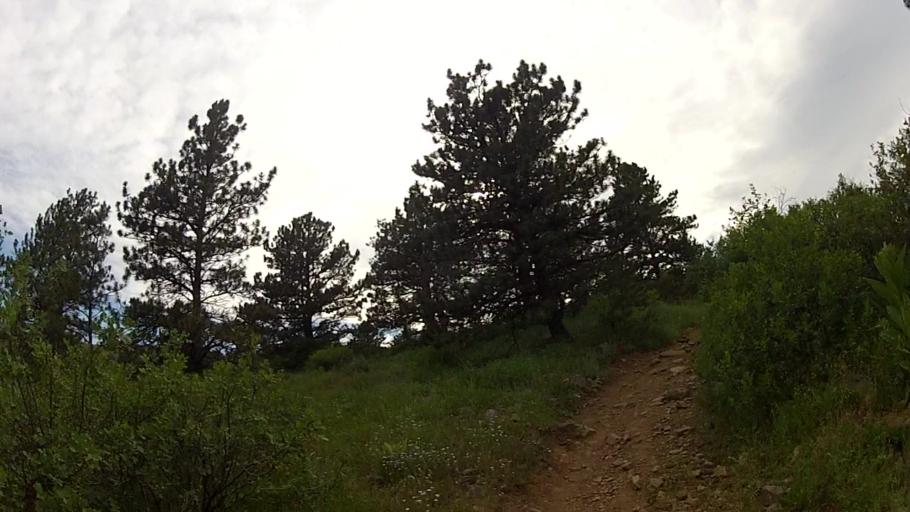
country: US
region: Colorado
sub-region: Larimer County
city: Laporte
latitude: 40.4840
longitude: -105.2371
